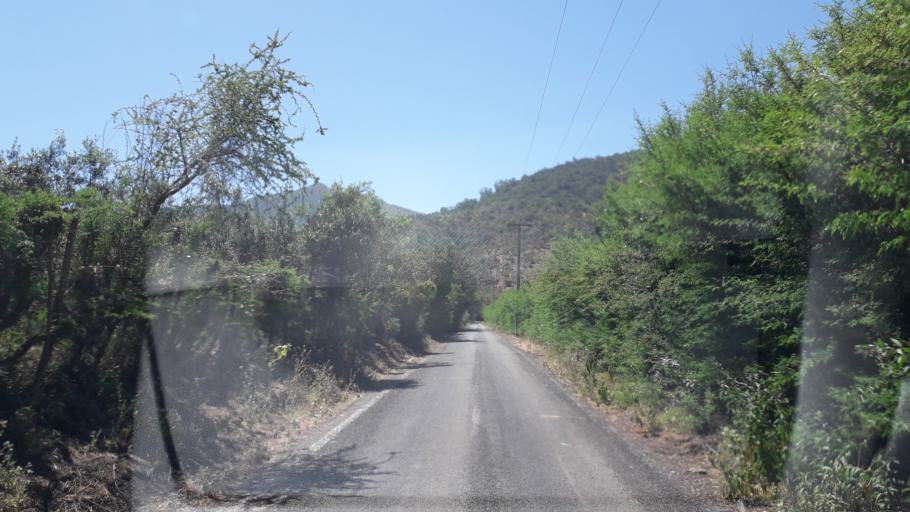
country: CL
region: Valparaiso
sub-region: Provincia de Marga Marga
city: Limache
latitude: -33.0738
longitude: -71.2148
